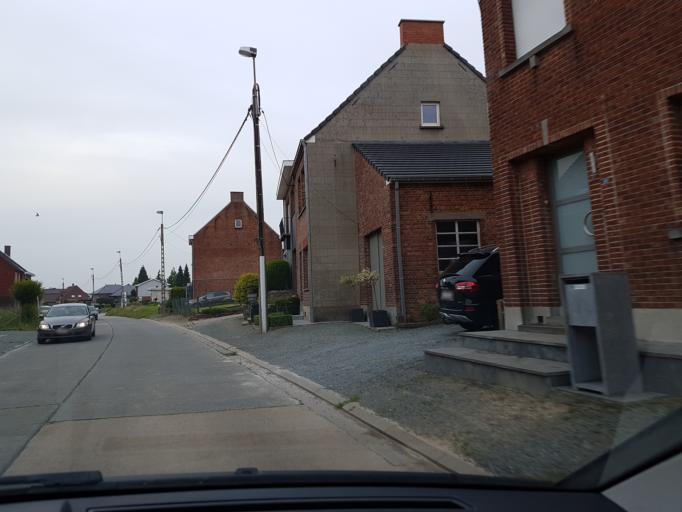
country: BE
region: Flanders
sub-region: Provincie Oost-Vlaanderen
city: Dendermonde
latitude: 50.9851
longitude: 4.0919
